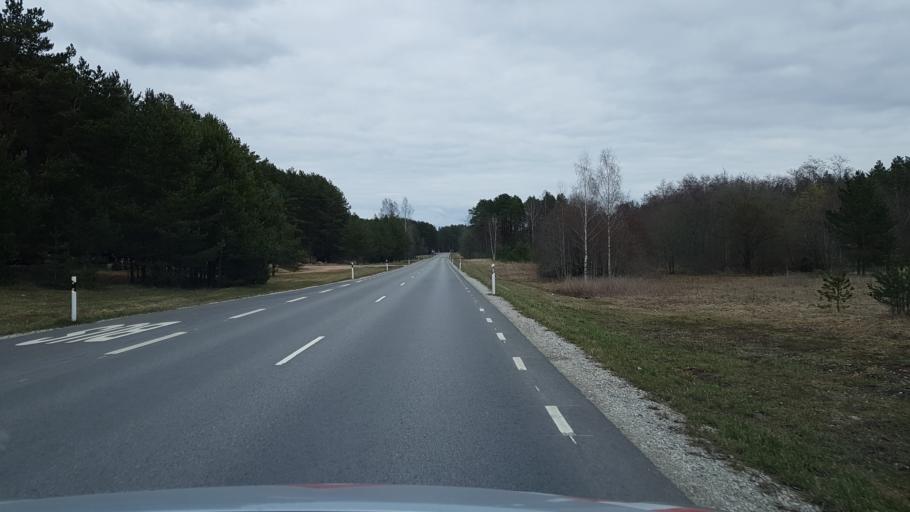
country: EE
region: Ida-Virumaa
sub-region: Narva-Joesuu linn
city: Narva-Joesuu
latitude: 59.4171
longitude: 28.0975
